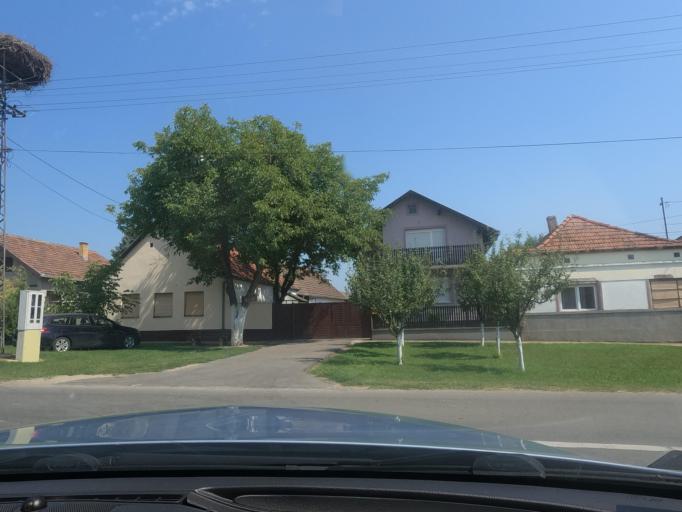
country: RS
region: Autonomna Pokrajina Vojvodina
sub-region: Juznobacki Okrug
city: Kovilj
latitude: 45.2205
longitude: 20.0353
